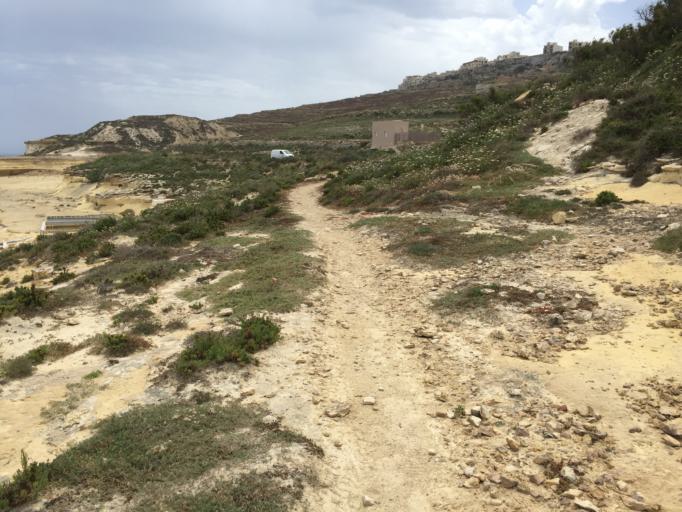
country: MT
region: Iz-Zebbug
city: Zebbug
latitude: 36.0809
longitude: 14.2332
